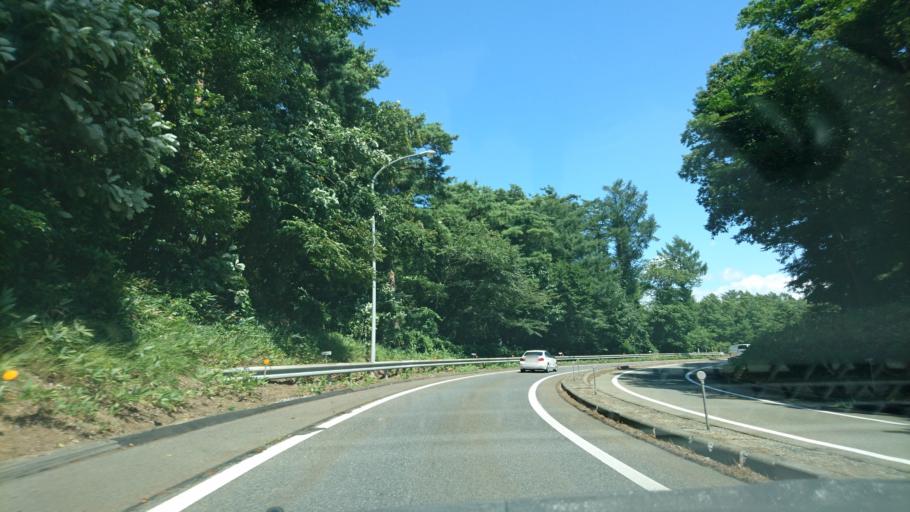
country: JP
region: Iwate
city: Morioka-shi
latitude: 39.7978
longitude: 141.1107
